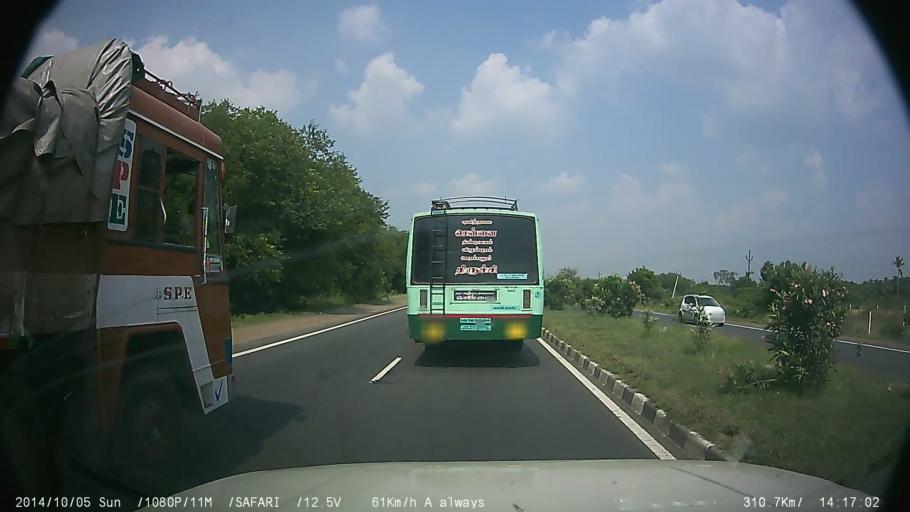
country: IN
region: Tamil Nadu
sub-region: Villupuram
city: Tindivanam
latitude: 12.2881
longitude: 79.7179
